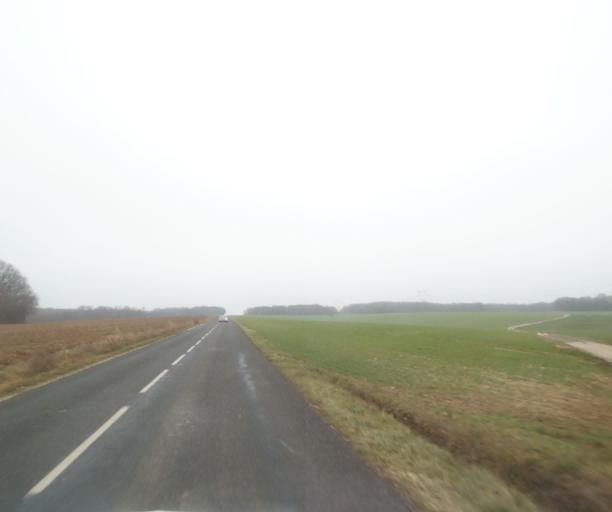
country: FR
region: Champagne-Ardenne
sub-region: Departement de la Haute-Marne
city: Bienville
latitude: 48.5215
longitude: 5.0579
